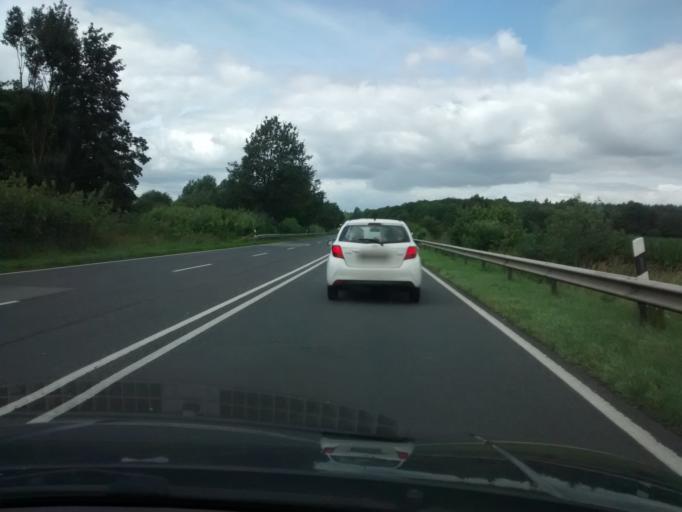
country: DE
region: Lower Saxony
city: Cappeln
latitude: 52.8491
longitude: 8.0983
